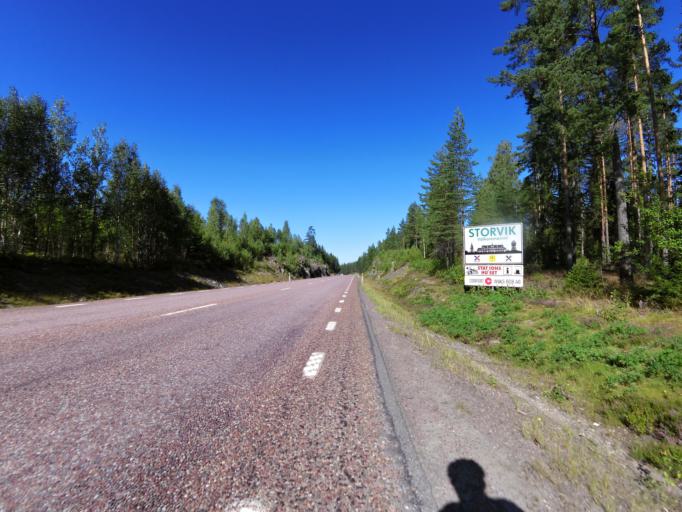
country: SE
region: Gaevleborg
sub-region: Hofors Kommun
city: Hofors
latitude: 60.5575
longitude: 16.4815
